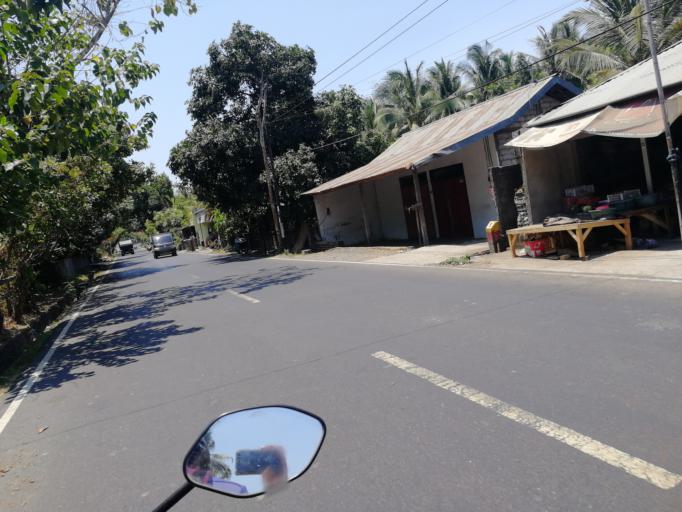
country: ID
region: Bali
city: Banjar Trunyan
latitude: -8.1499
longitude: 115.4094
